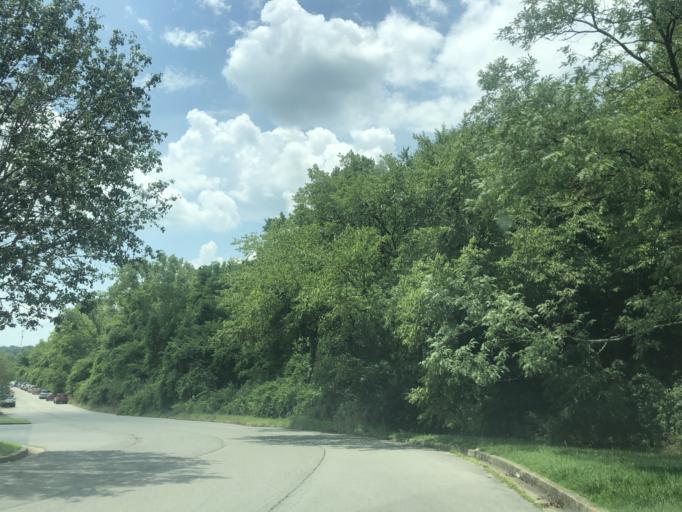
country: US
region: Tennessee
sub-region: Rutherford County
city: La Vergne
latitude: 36.0536
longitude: -86.6586
